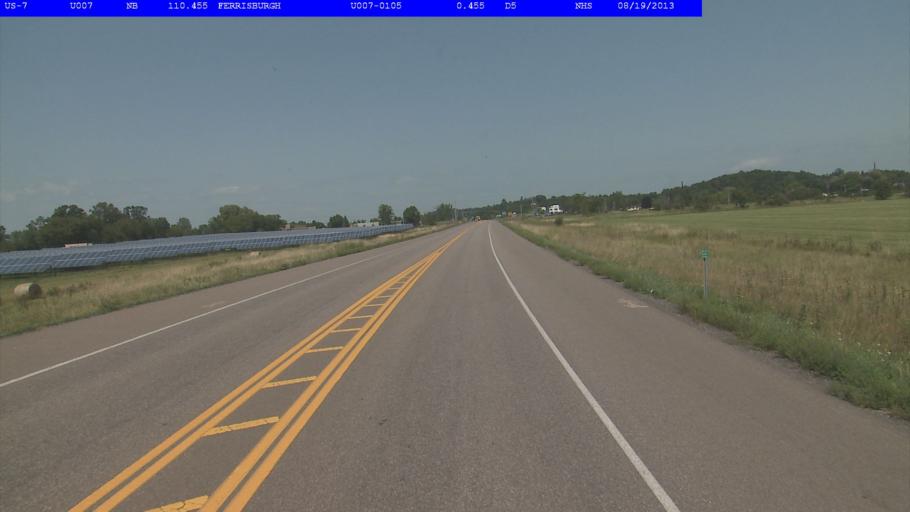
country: US
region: Vermont
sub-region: Addison County
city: Vergennes
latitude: 44.1683
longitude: -73.2394
